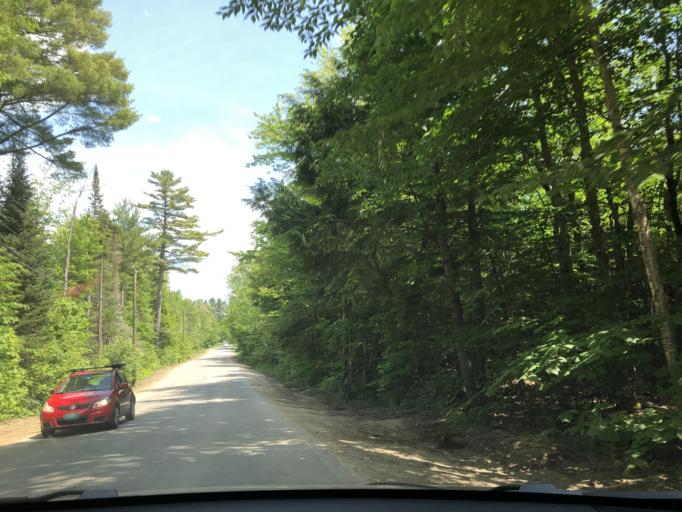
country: US
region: New Hampshire
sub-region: Merrimack County
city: New London
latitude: 43.4087
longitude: -71.9957
